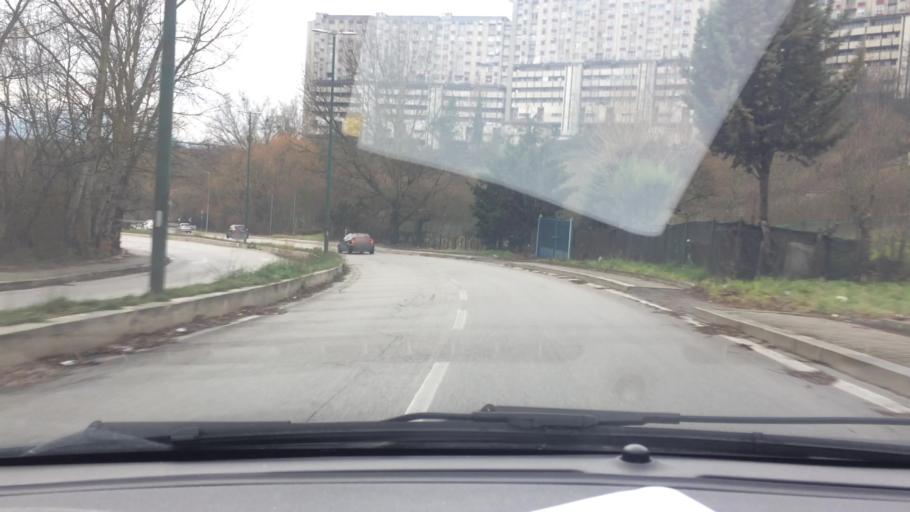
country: IT
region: Basilicate
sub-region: Provincia di Potenza
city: Potenza
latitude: 40.6335
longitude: 15.7942
